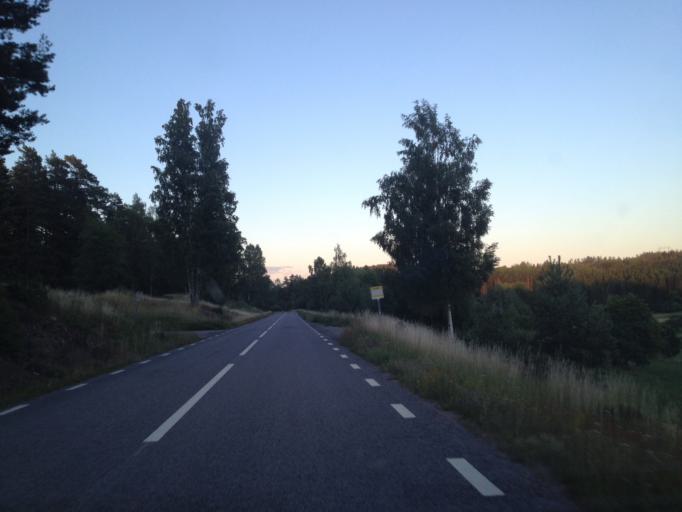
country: SE
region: Kalmar
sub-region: Vasterviks Kommun
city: Overum
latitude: 58.0239
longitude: 16.1200
